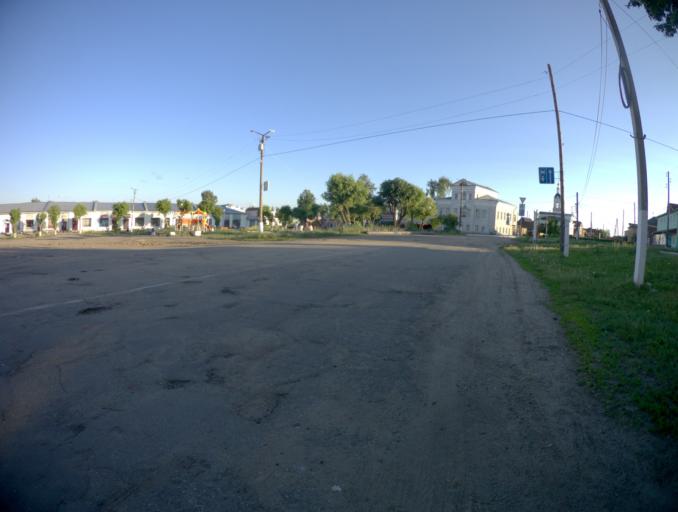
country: RU
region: Ivanovo
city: Gavrilov Posad
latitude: 56.5588
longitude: 40.1205
